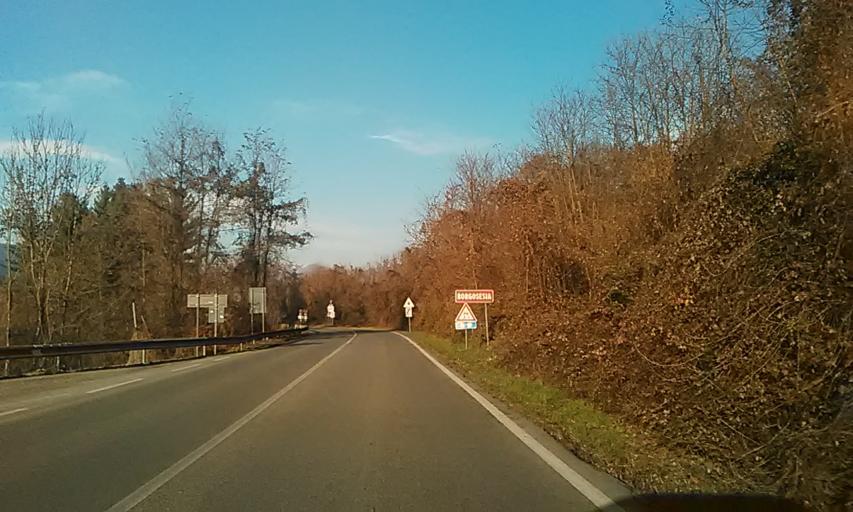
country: IT
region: Piedmont
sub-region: Provincia di Vercelli
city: Quarona
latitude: 45.7455
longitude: 8.2640
